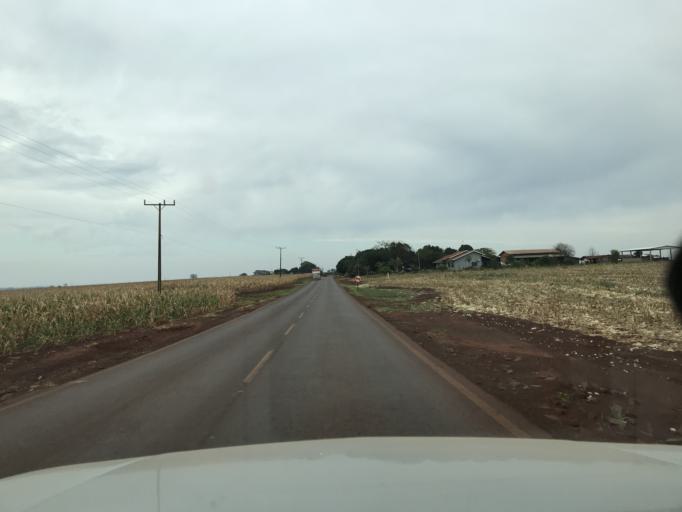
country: BR
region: Parana
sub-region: Palotina
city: Palotina
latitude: -24.4188
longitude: -53.8744
